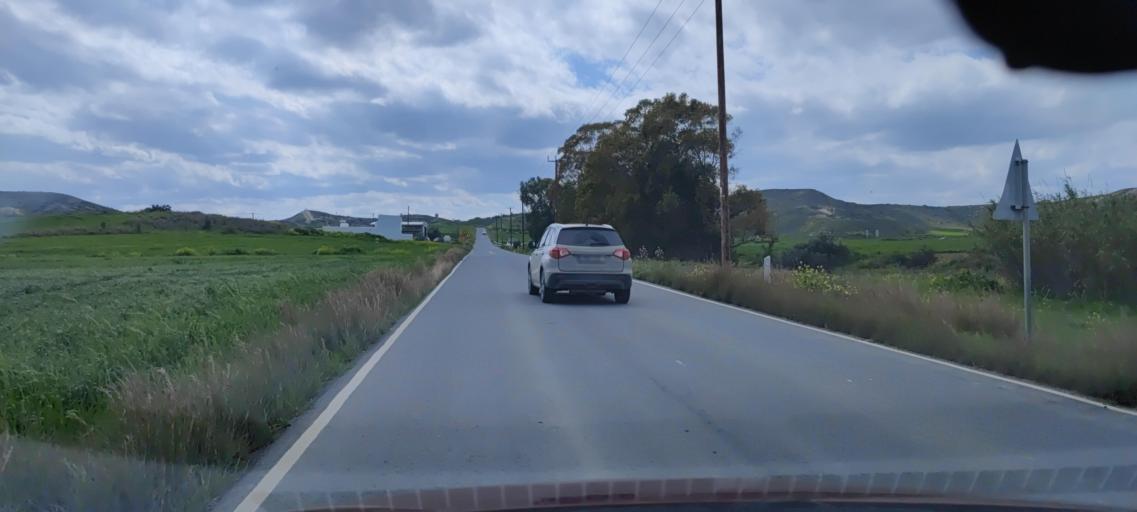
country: CY
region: Lefkosia
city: Tseri
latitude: 35.0404
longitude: 33.3166
